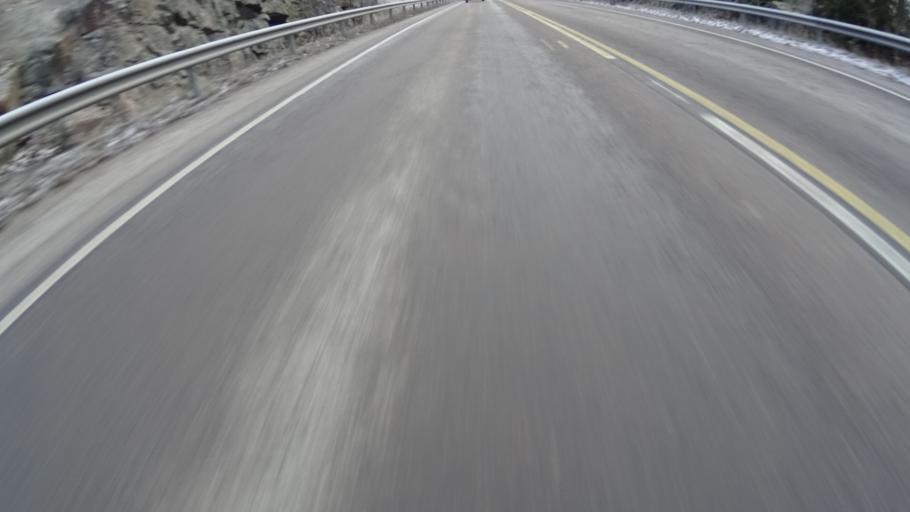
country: FI
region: Uusimaa
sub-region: Helsinki
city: Nurmijaervi
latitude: 60.4310
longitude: 24.7208
